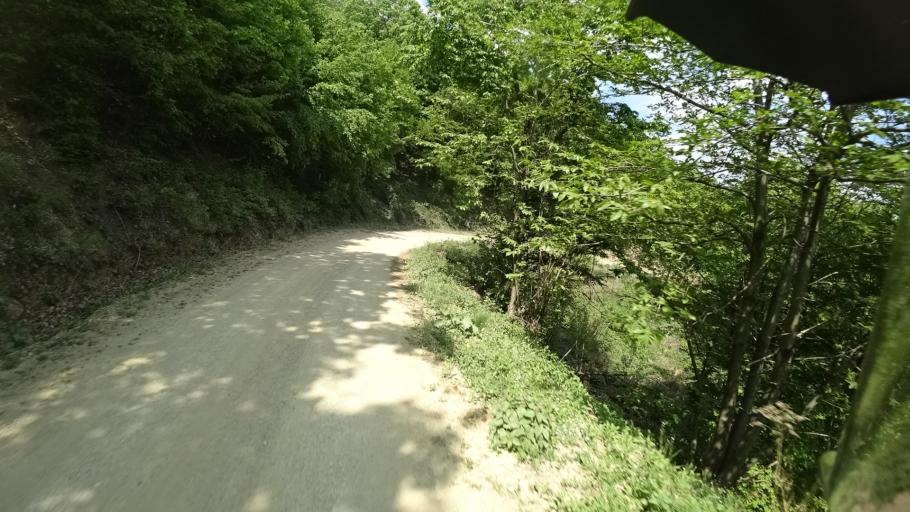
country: HR
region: Grad Zagreb
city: Kasina
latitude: 45.8833
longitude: 15.9924
